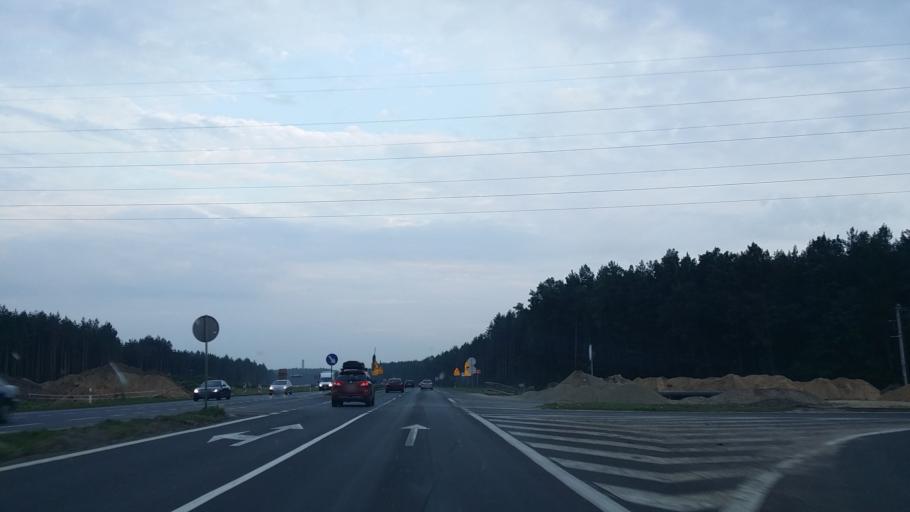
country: PL
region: Lower Silesian Voivodeship
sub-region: Powiat polkowicki
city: Polkowice
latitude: 51.4505
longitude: 16.1329
